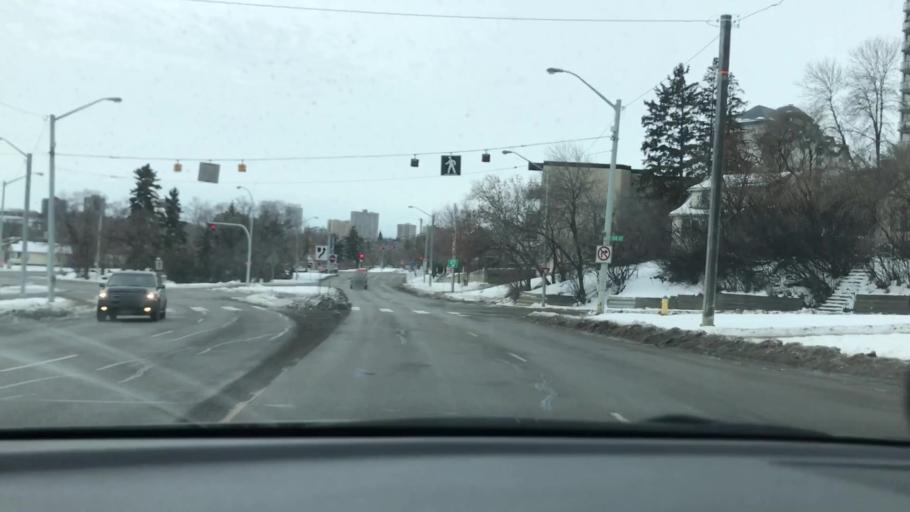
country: CA
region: Alberta
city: Edmonton
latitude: 53.5355
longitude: -113.4970
